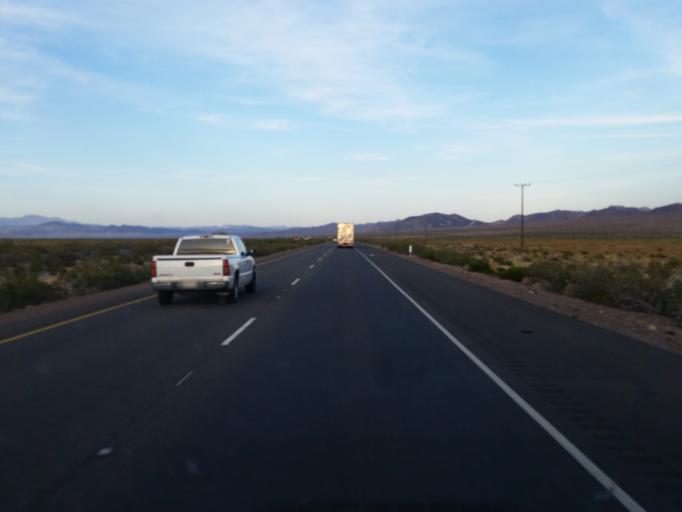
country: US
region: California
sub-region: San Bernardino County
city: Joshua Tree
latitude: 34.7341
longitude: -116.2926
